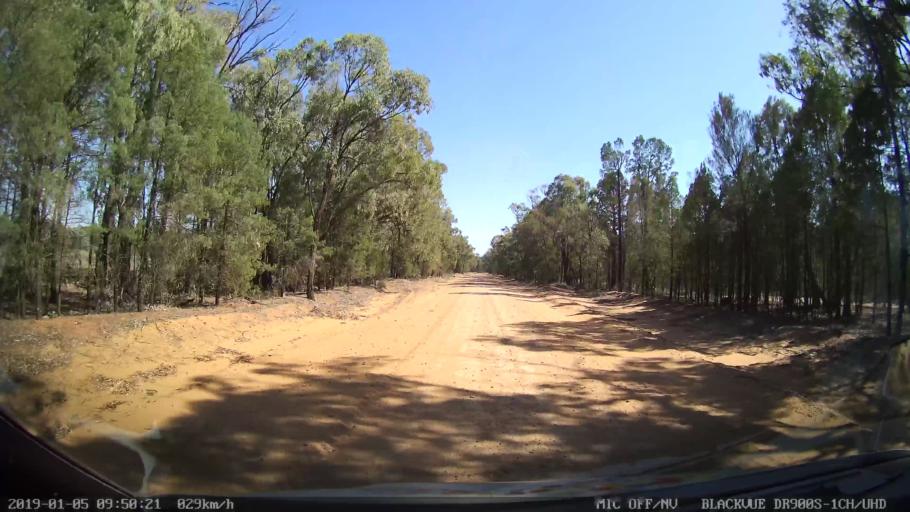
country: AU
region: New South Wales
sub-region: Gilgandra
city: Gilgandra
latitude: -31.6649
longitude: 148.7588
